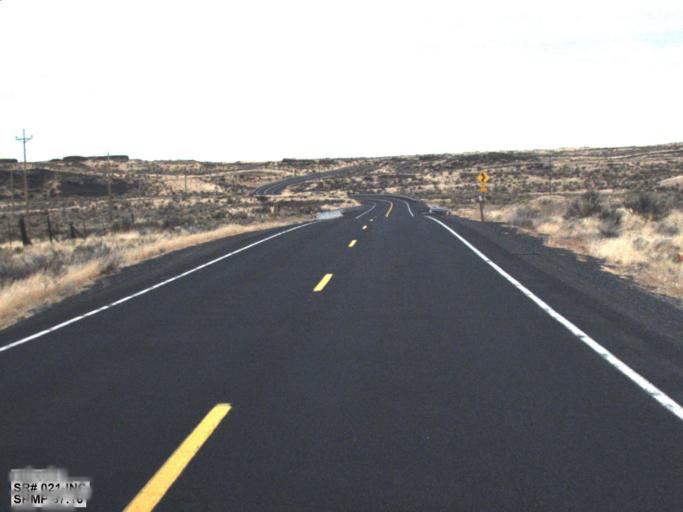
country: US
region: Washington
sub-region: Adams County
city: Ritzville
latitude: 47.4634
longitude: -118.7647
